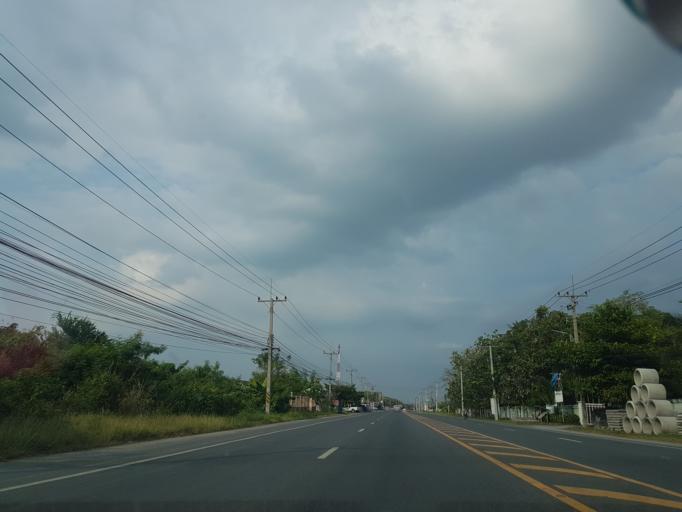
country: TH
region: Sara Buri
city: Phra Phutthabat
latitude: 14.6864
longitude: 100.7758
